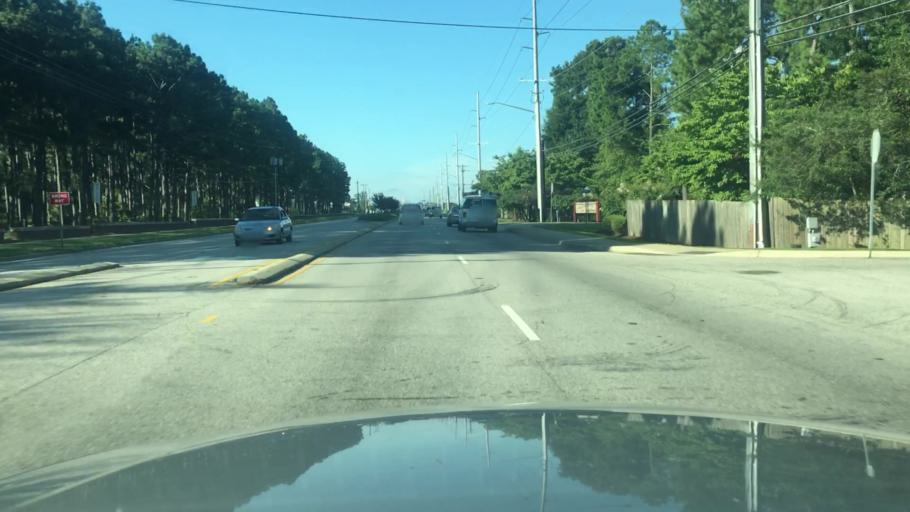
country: US
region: North Carolina
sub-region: Cumberland County
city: Fayetteville
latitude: 35.1353
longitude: -78.8763
